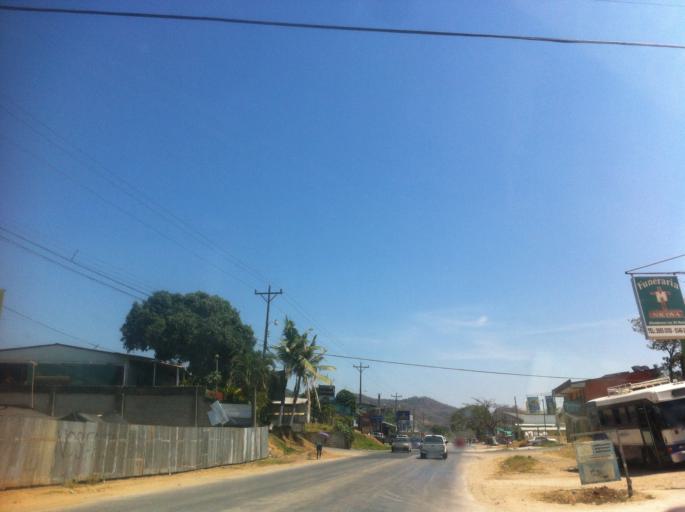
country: CR
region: Guanacaste
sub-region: Canton de Nicoya
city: Nicoya
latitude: 10.1500
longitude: -85.4526
